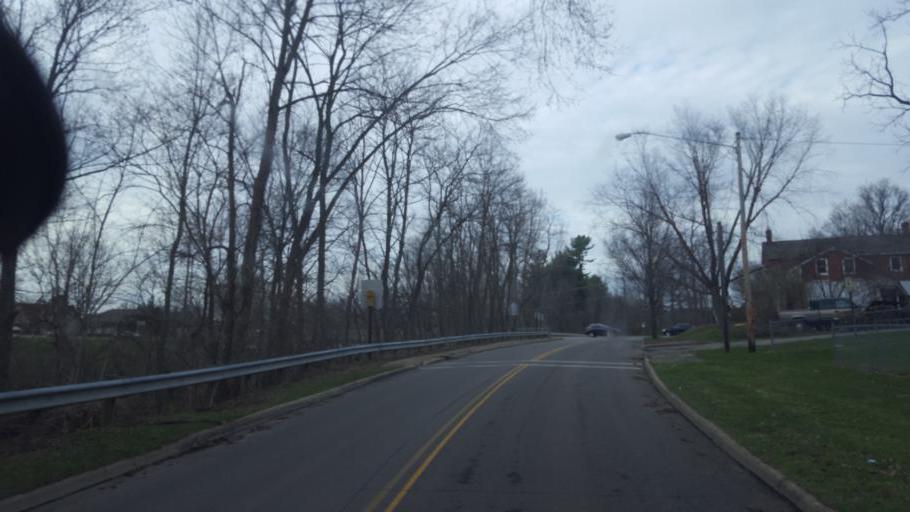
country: US
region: Ohio
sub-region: Richland County
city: Lexington
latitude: 40.6777
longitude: -82.5791
